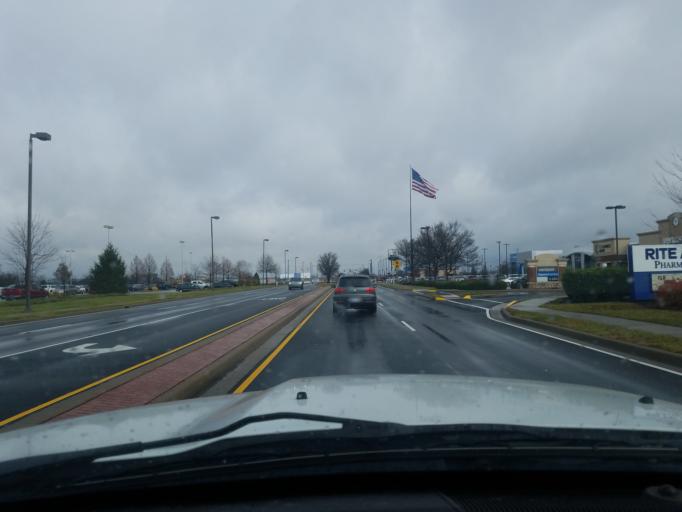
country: US
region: Indiana
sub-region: Clark County
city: Clarksville
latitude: 38.3262
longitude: -85.7644
